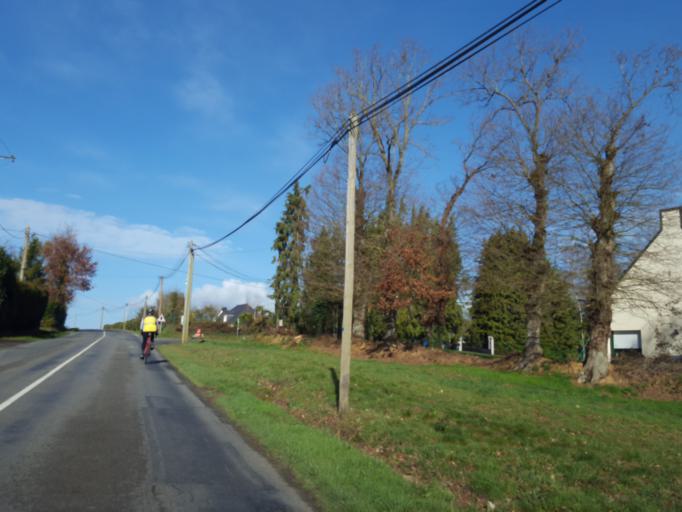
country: FR
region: Brittany
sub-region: Departement d'Ille-et-Vilaine
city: Chavagne
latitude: 48.0304
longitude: -1.7965
